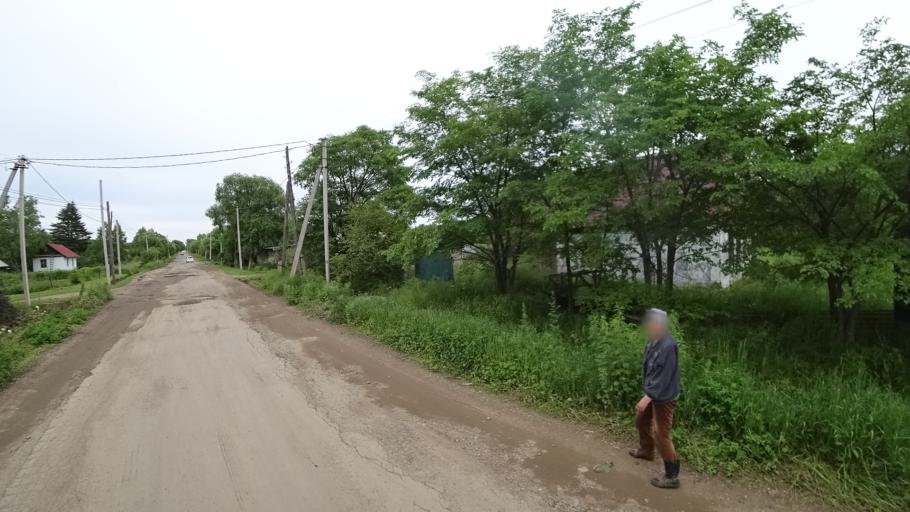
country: RU
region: Primorskiy
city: Novosysoyevka
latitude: 44.2070
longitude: 133.3304
